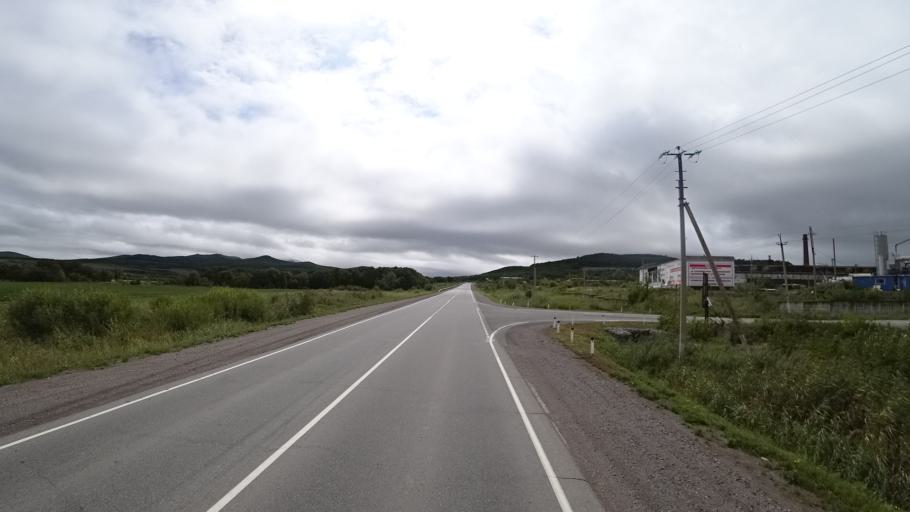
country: RU
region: Primorskiy
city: Monastyrishche
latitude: 44.1698
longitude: 132.4410
